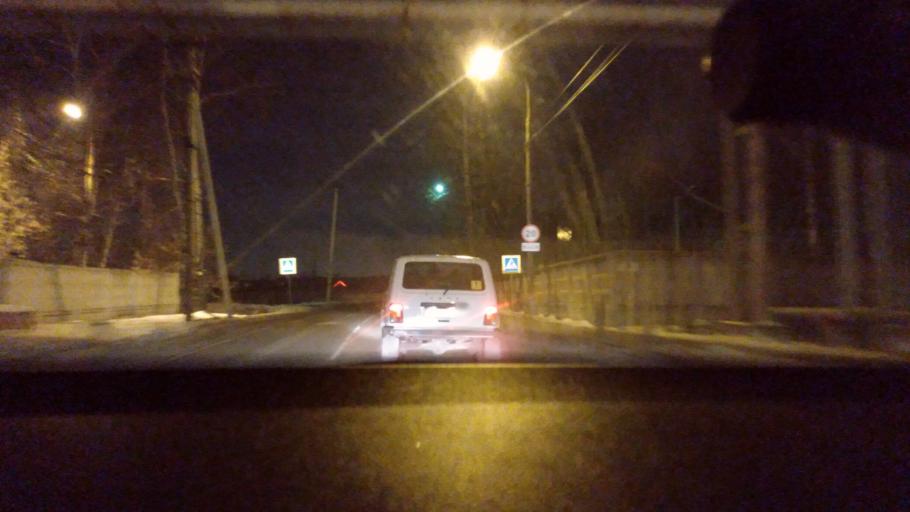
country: RU
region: Moskovskaya
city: Rodniki
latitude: 55.6793
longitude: 38.1049
